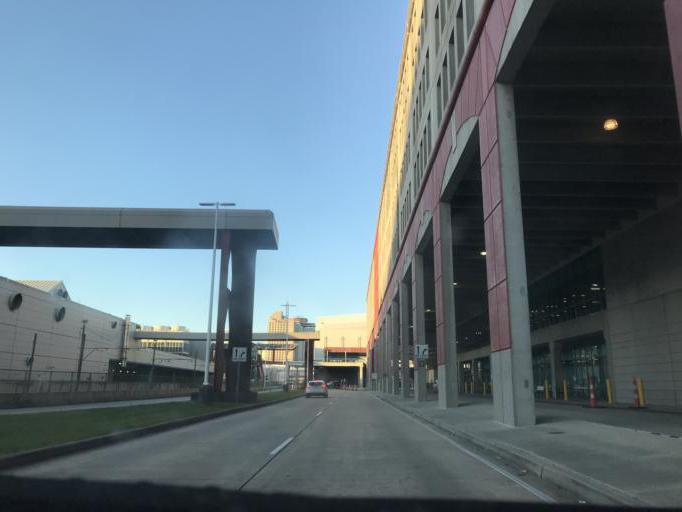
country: US
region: Louisiana
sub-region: Orleans Parish
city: New Orleans
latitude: 29.9395
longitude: -90.0617
